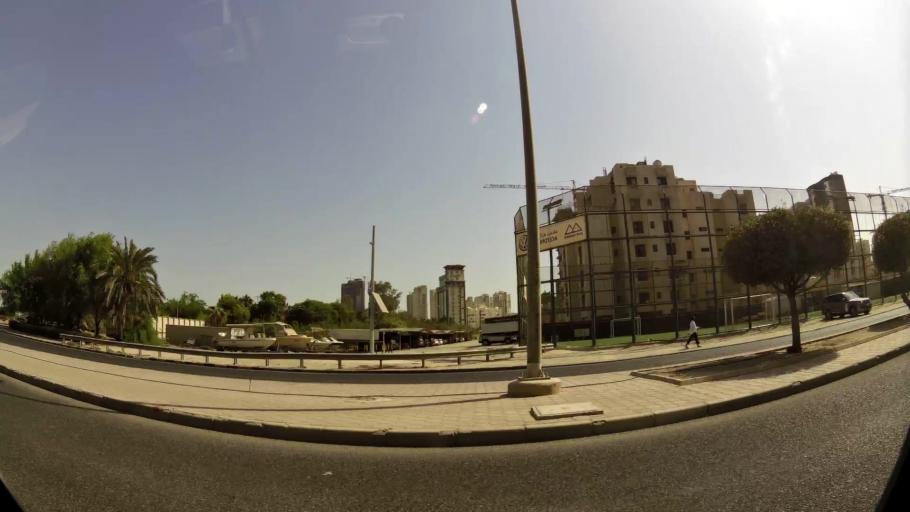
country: KW
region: Muhafazat Hawalli
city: Hawalli
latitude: 29.3405
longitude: 48.0485
